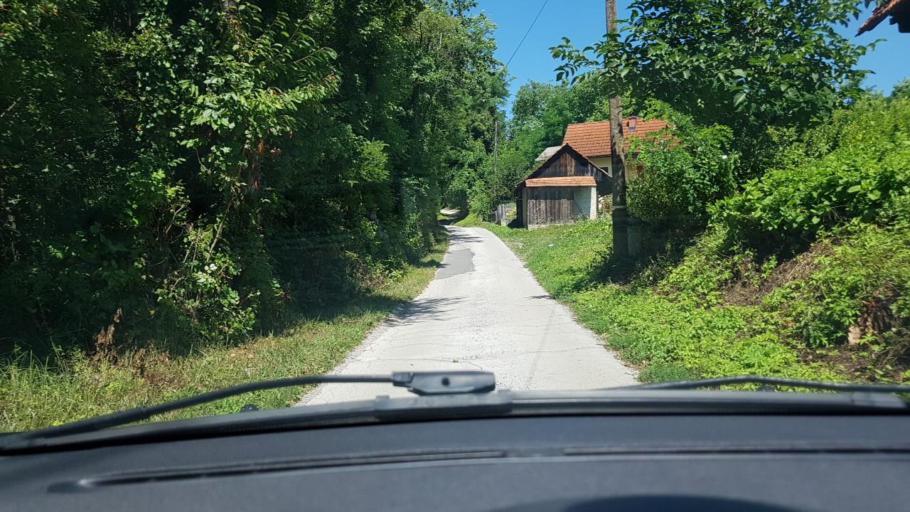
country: HR
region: Krapinsko-Zagorska
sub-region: Grad Krapina
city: Krapina
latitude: 46.1094
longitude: 15.8517
